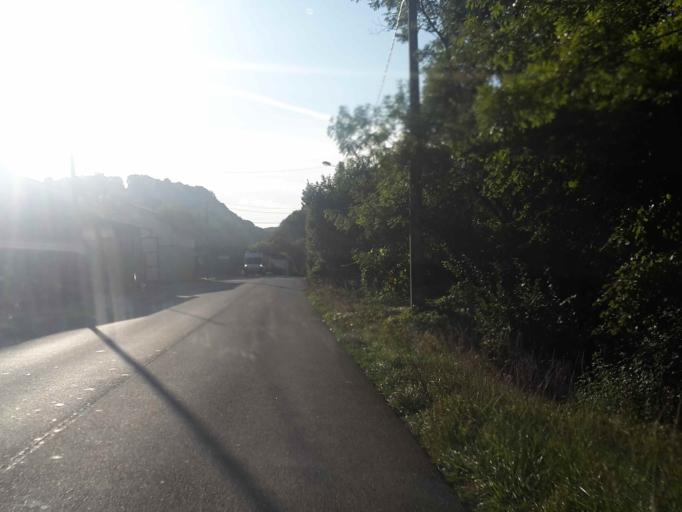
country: FR
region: Franche-Comte
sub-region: Departement du Doubs
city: Baume-les-Dames
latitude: 47.3413
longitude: 6.3647
